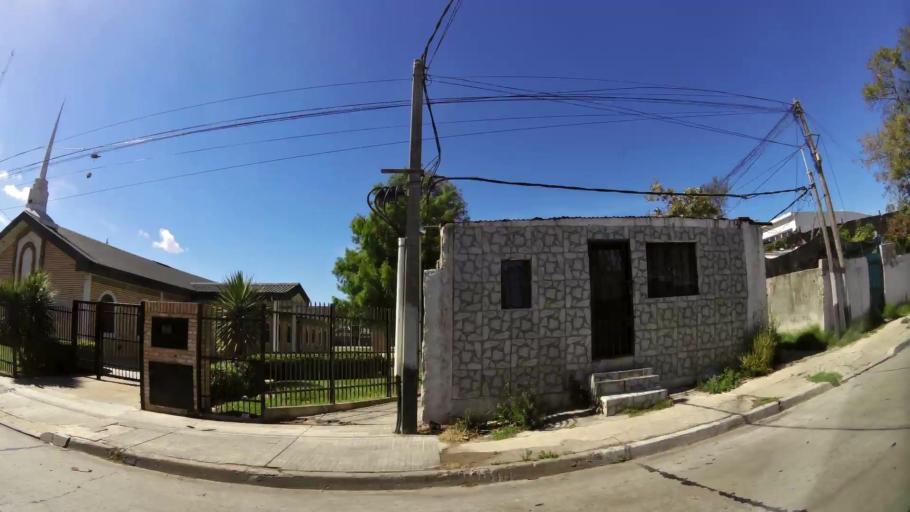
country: UY
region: Canelones
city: Paso de Carrasco
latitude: -34.8467
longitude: -56.1287
